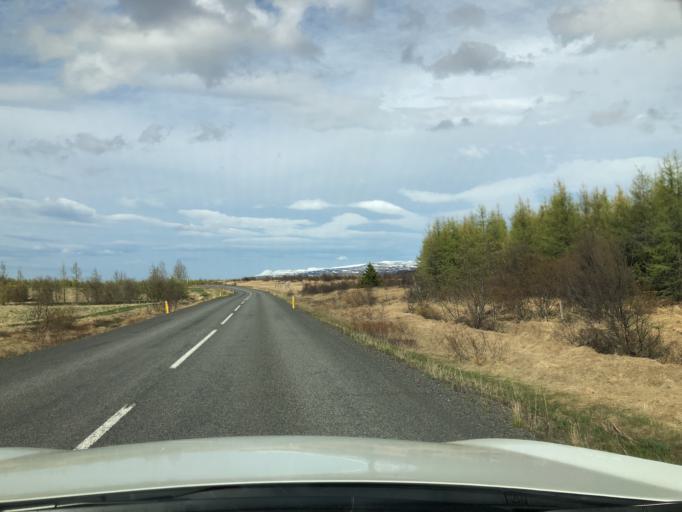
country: IS
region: East
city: Egilsstadir
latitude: 65.1864
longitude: -14.5012
